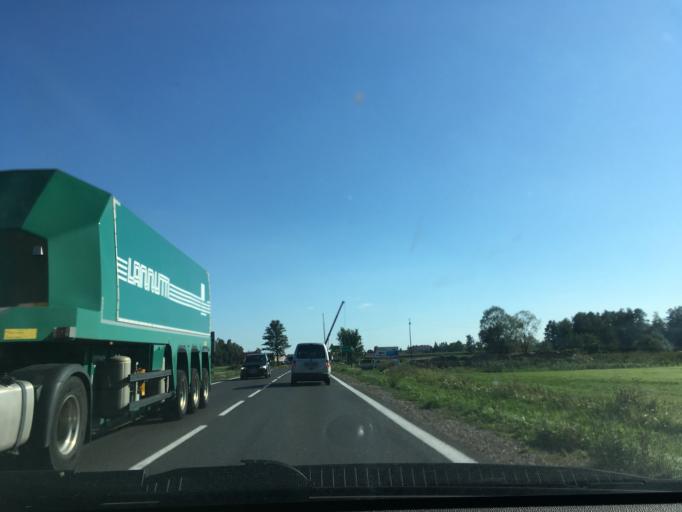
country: PL
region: Podlasie
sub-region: Powiat sokolski
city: Suchowola
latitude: 53.4570
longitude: 23.0881
